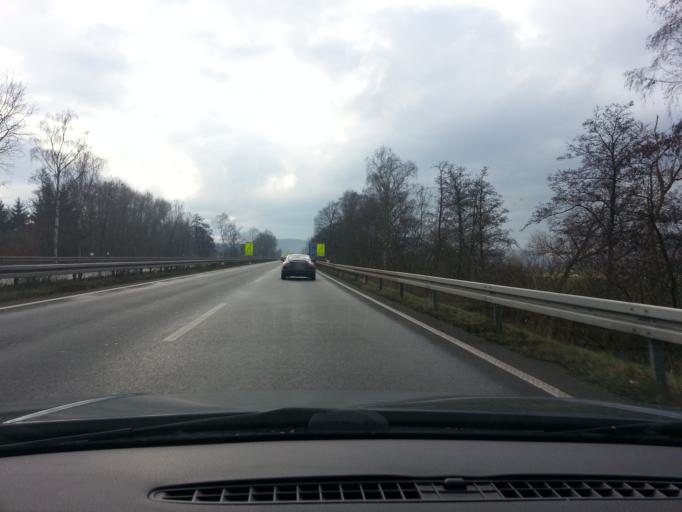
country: DE
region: Saarland
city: Homburg
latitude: 49.2790
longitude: 7.3125
